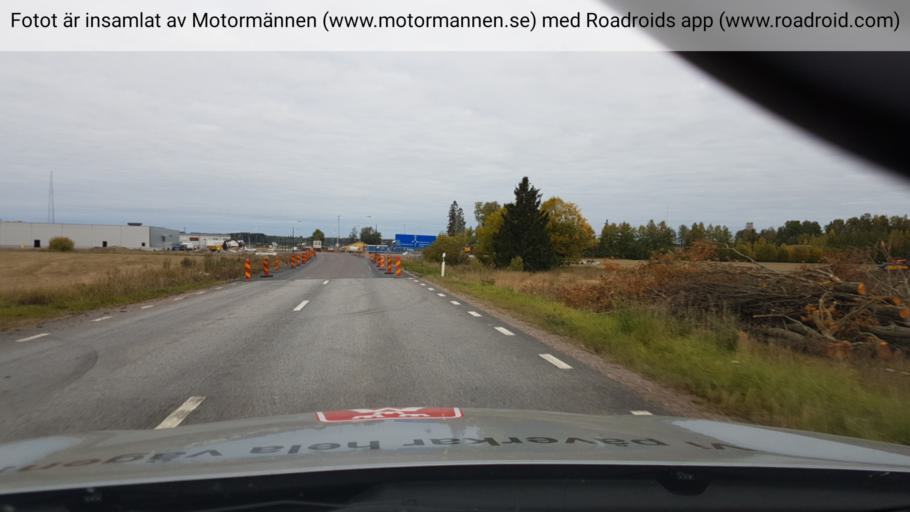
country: SE
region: Uppsala
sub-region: Tierps Kommun
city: Tierp
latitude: 60.3432
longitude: 17.4974
